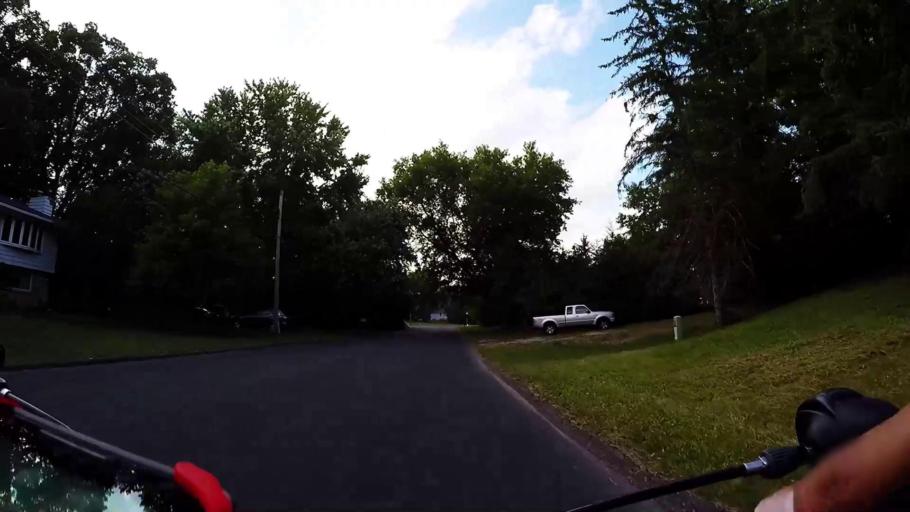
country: US
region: Minnesota
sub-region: Hennepin County
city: Eden Prairie
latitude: 44.8831
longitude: -93.4789
